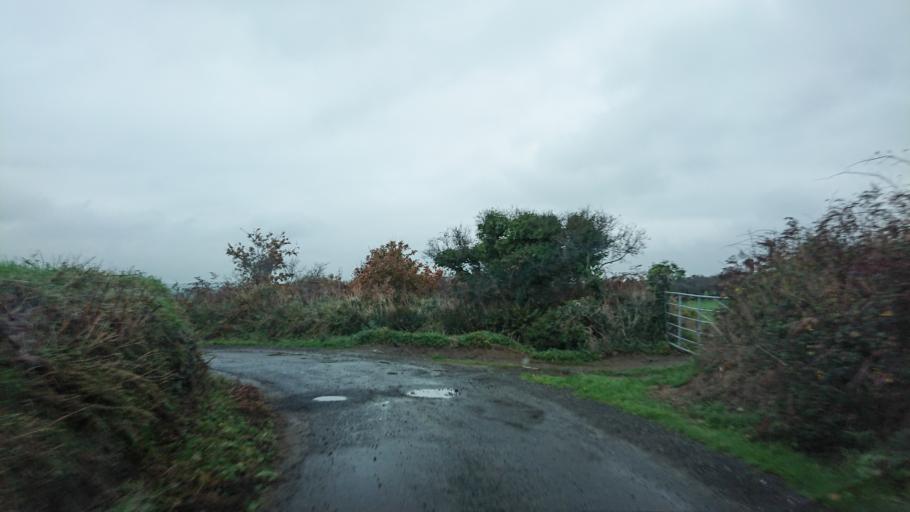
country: IE
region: Munster
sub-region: Waterford
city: Tra Mhor
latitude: 52.1985
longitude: -7.1501
